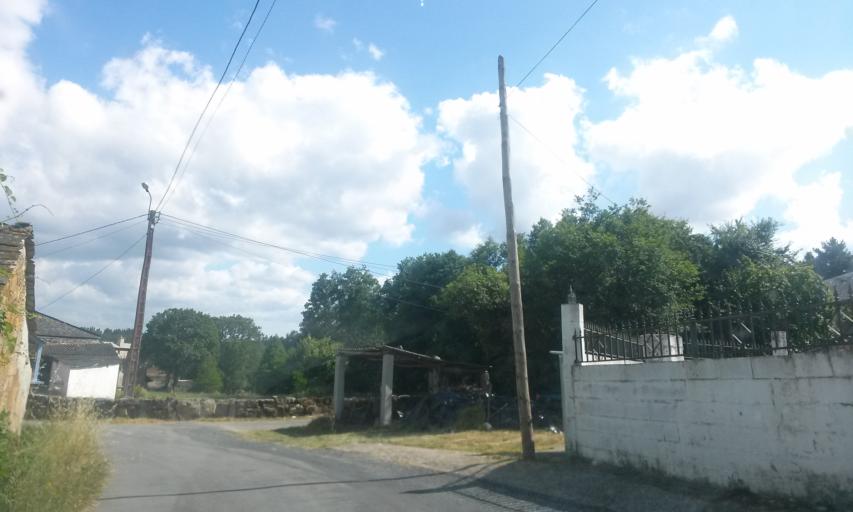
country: ES
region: Galicia
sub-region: Provincia de Lugo
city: Begonte
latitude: 43.1185
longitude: -7.6722
